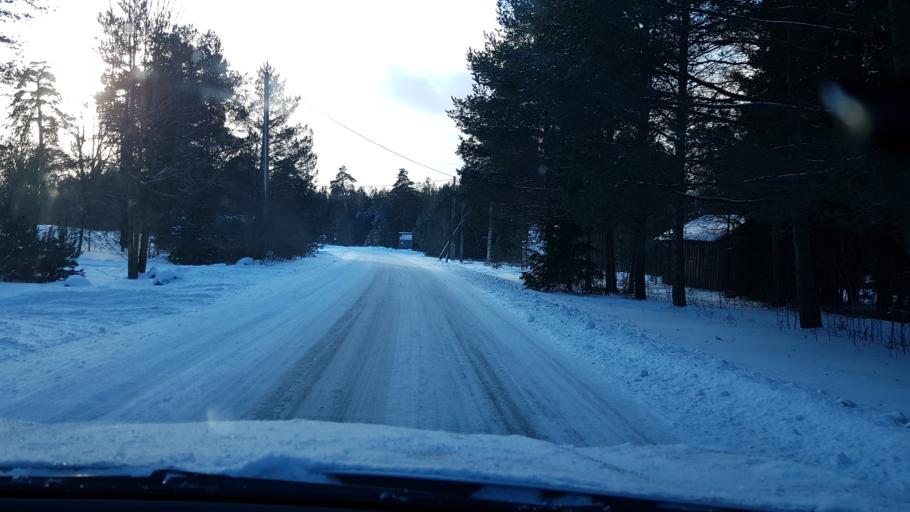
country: EE
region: Harju
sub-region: Nissi vald
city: Turba
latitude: 59.2256
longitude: 24.1628
